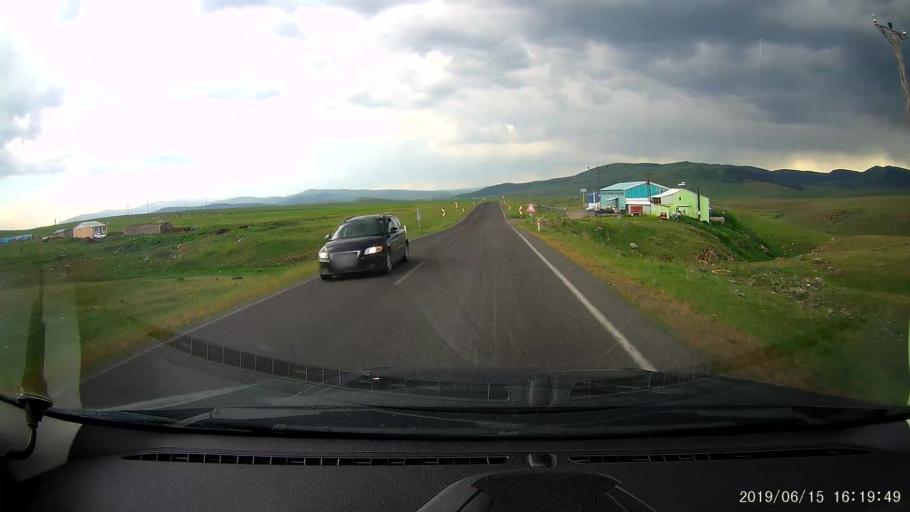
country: TR
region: Ardahan
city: Hanak
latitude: 41.2244
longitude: 42.8500
